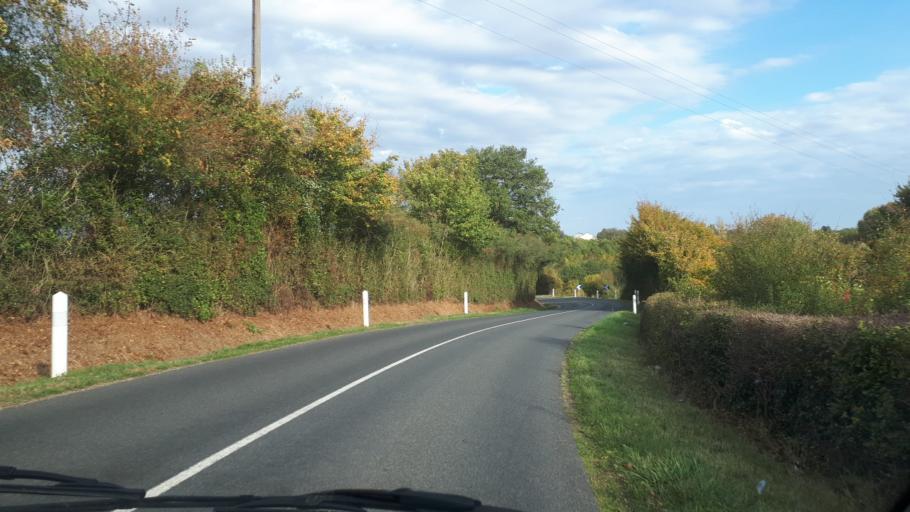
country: FR
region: Centre
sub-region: Departement du Loir-et-Cher
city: Mondoubleau
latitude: 47.9729
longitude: 0.9195
